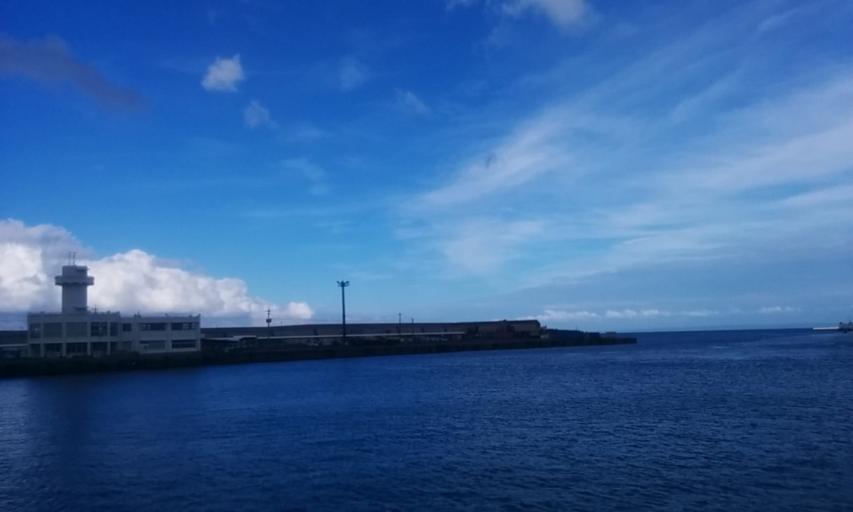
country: JP
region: Kagoshima
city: Nishinoomote
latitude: 30.4312
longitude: 130.5712
